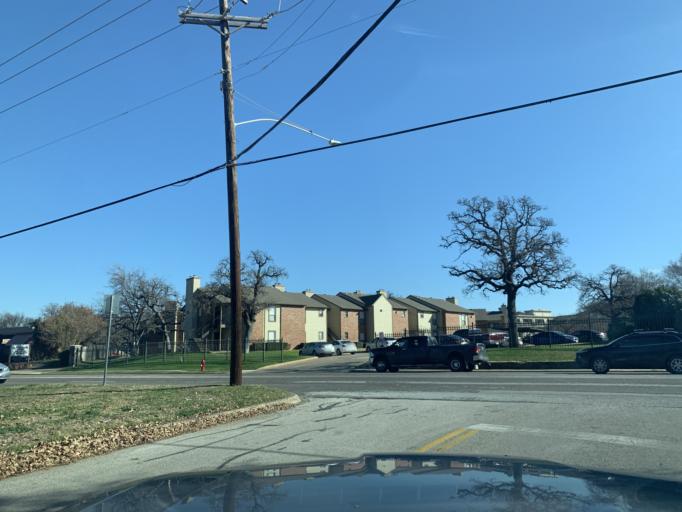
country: US
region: Texas
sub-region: Tarrant County
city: Bedford
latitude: 32.8407
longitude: -97.1486
